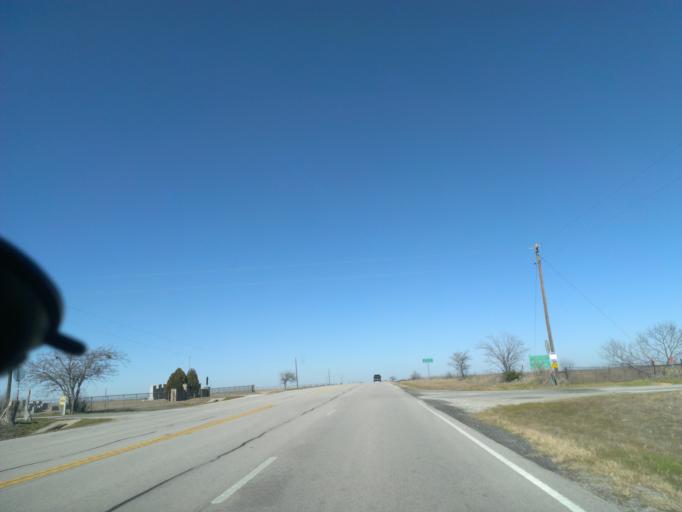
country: US
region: Texas
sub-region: Williamson County
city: Florence
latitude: 30.8598
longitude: -97.9113
